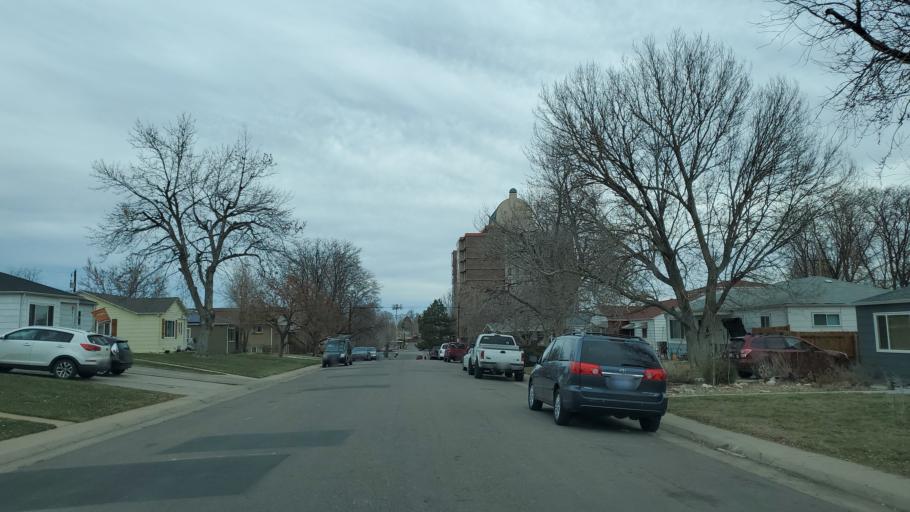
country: US
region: Colorado
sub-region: Arapahoe County
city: Sheridan
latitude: 39.6941
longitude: -105.0088
